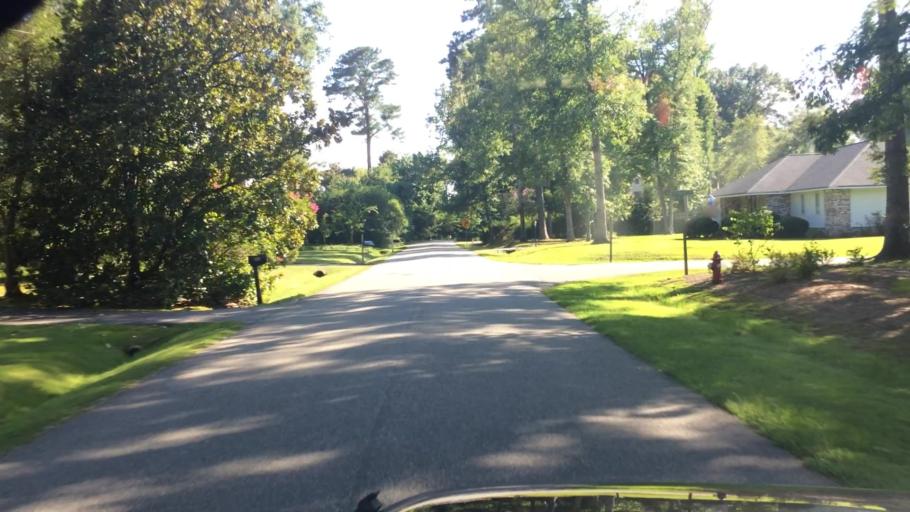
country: US
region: Virginia
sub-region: James City County
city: Williamsburg
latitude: 37.2368
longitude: -76.7983
